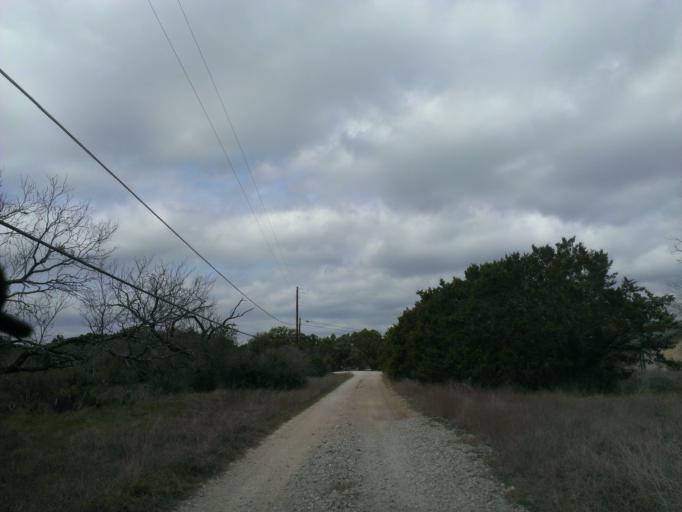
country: US
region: Texas
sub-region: Travis County
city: Briarcliff
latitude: 30.3891
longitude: -98.0923
